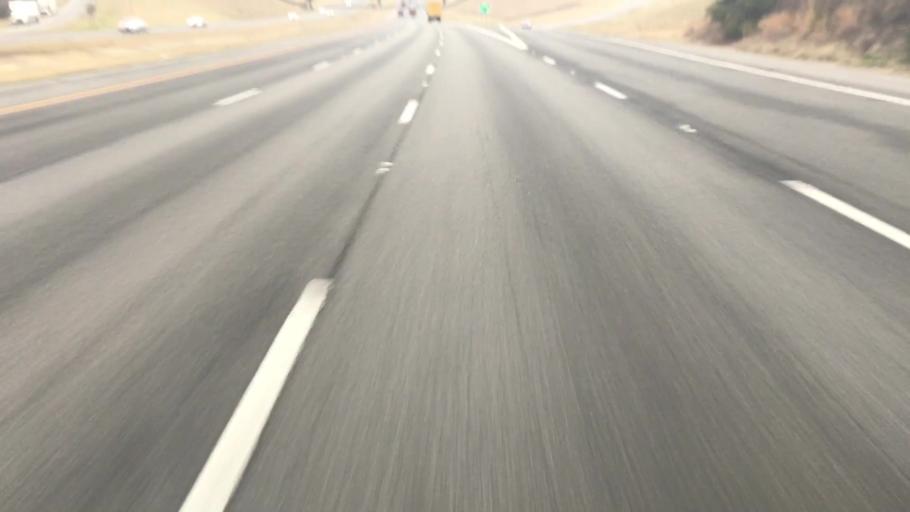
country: US
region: Alabama
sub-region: Jefferson County
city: Forestdale
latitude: 33.5943
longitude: -86.8813
